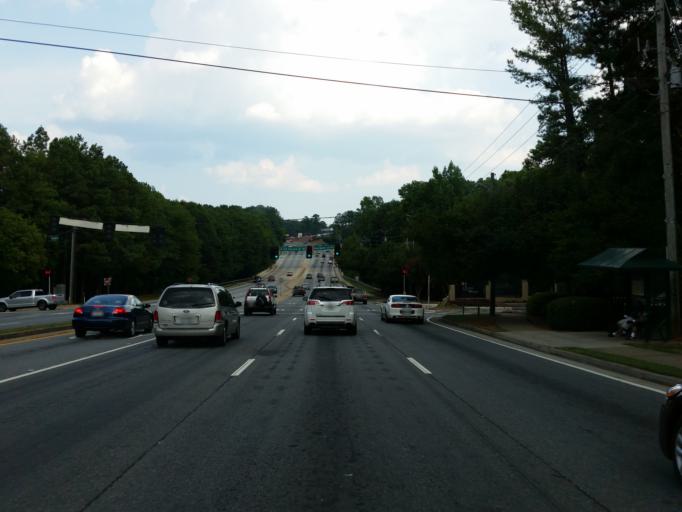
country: US
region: Georgia
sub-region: Fulton County
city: Roswell
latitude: 34.0263
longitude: -84.3330
